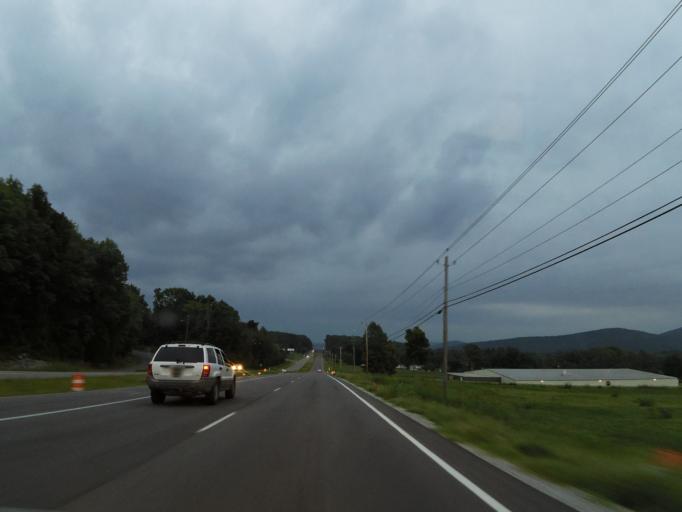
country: US
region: Alabama
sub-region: Madison County
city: Moores Mill
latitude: 34.7680
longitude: -86.4921
